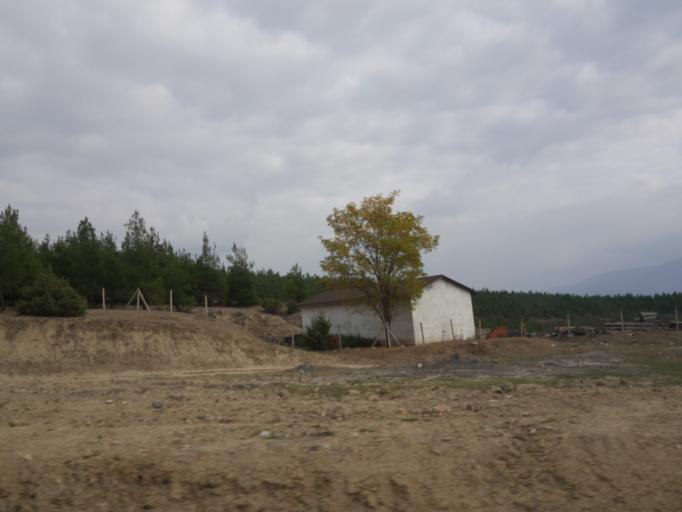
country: TR
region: Sinop
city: Duragan
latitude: 41.4326
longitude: 35.0543
